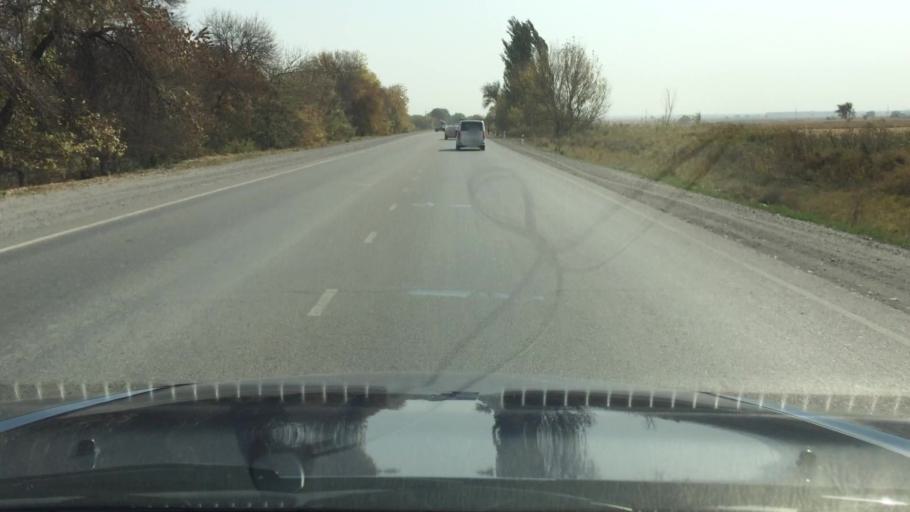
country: KG
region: Chuy
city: Lebedinovka
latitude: 42.9271
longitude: 74.6974
